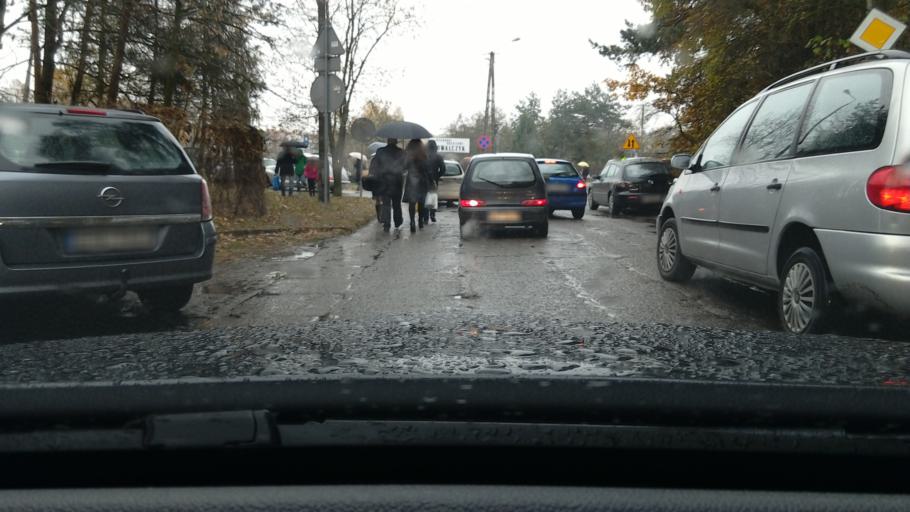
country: PL
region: Lodz Voivodeship
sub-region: Skierniewice
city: Skierniewice
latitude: 51.9348
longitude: 20.1586
